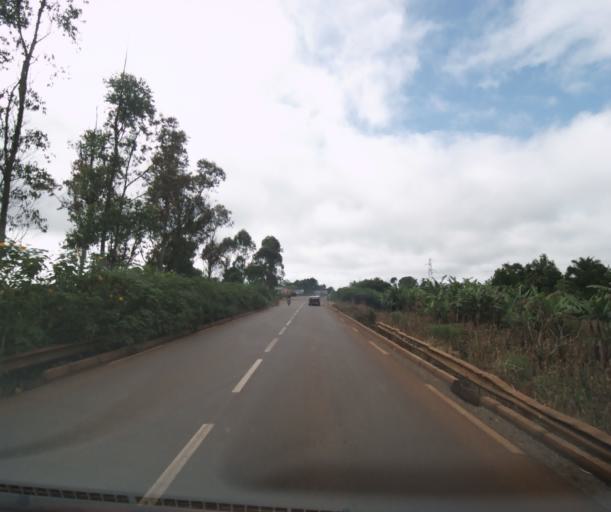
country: CM
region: West
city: Bansoa
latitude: 5.5258
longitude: 10.3396
